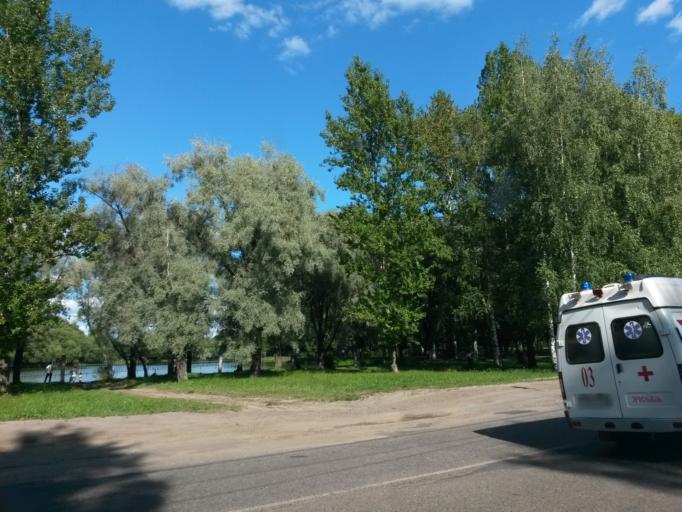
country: RU
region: Jaroslavl
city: Yaroslavl
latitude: 57.5826
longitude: 39.8491
